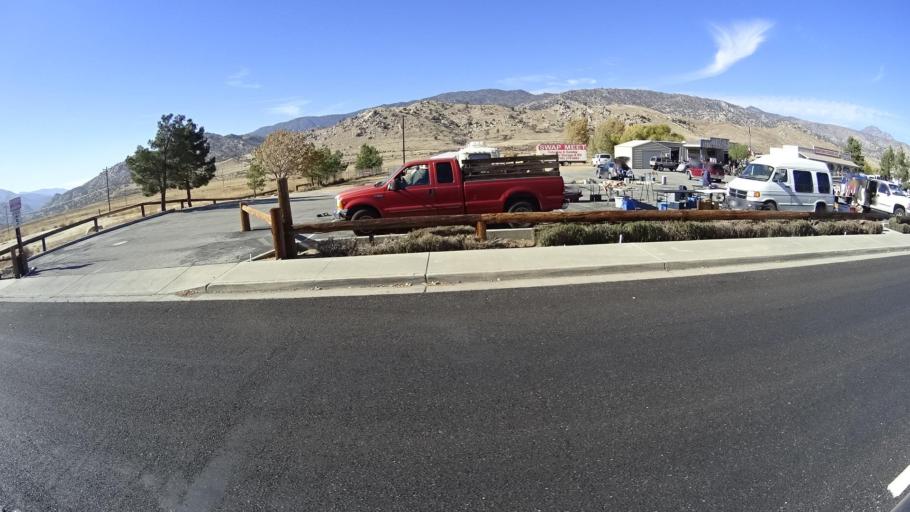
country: US
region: California
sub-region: Kern County
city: Lake Isabella
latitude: 35.6228
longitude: -118.4754
